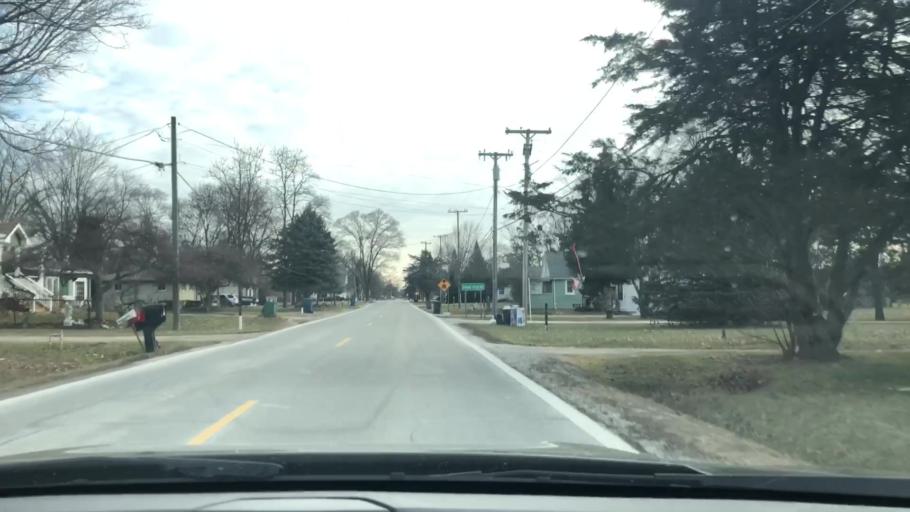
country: US
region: Michigan
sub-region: Macomb County
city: Romeo
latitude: 42.7308
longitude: -82.9627
